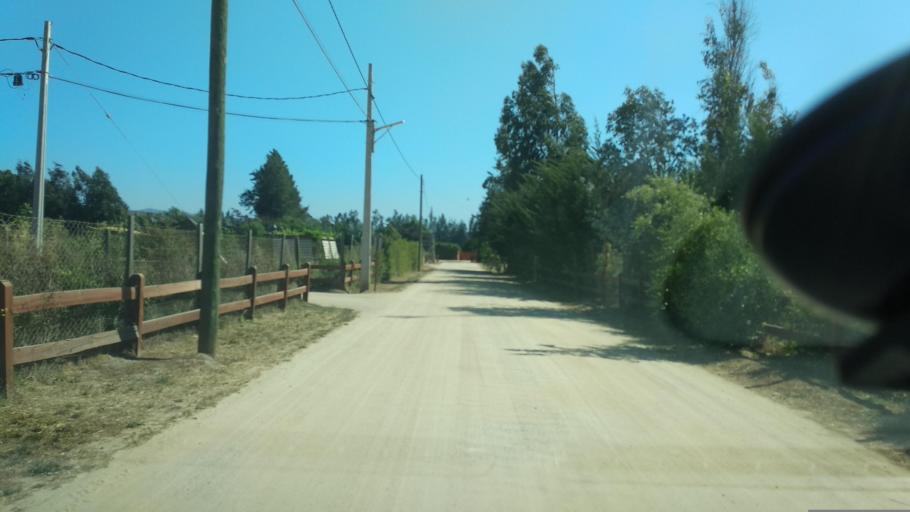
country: CL
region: Valparaiso
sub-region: Provincia de Marga Marga
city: Limache
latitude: -32.9733
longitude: -71.3097
